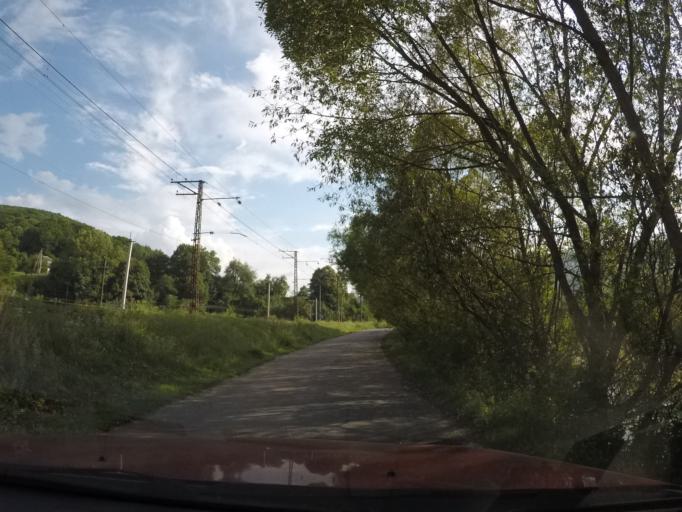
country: UA
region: Zakarpattia
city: Velykyi Bereznyi
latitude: 48.9939
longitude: 22.6398
